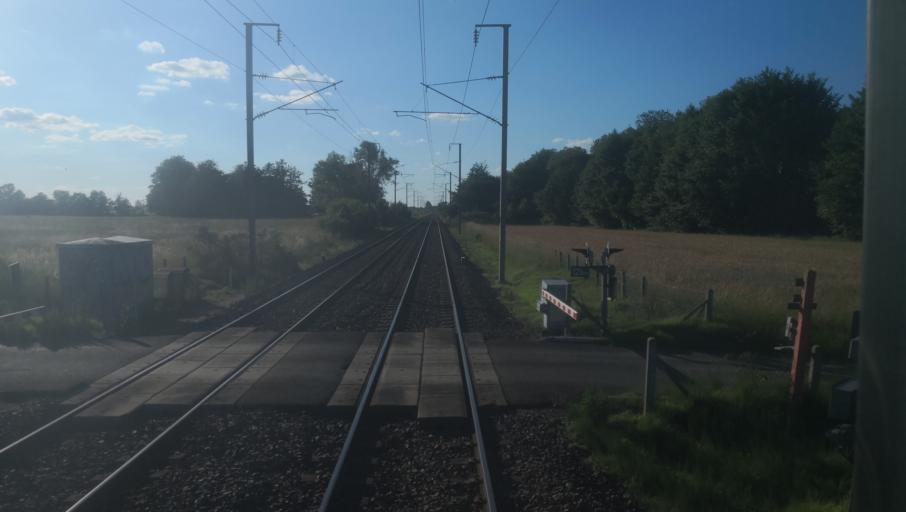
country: FR
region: Bourgogne
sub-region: Departement de la Nievre
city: Chantenay-Saint-Imbert
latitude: 46.6953
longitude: 3.2097
